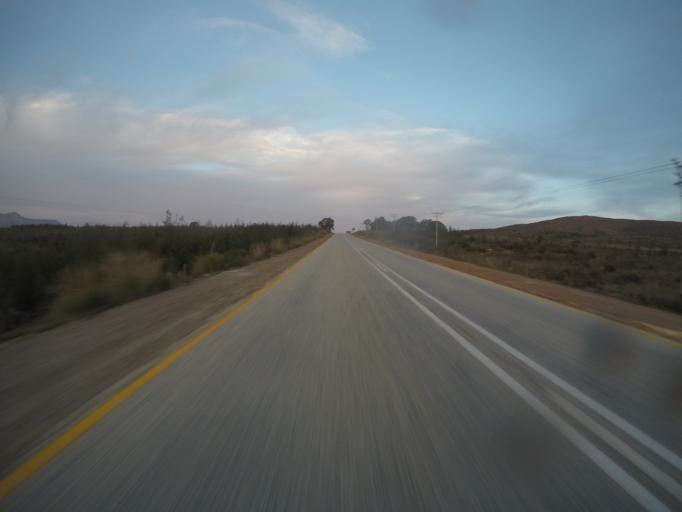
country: ZA
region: Western Cape
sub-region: Eden District Municipality
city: Plettenberg Bay
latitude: -33.7400
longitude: 23.4322
